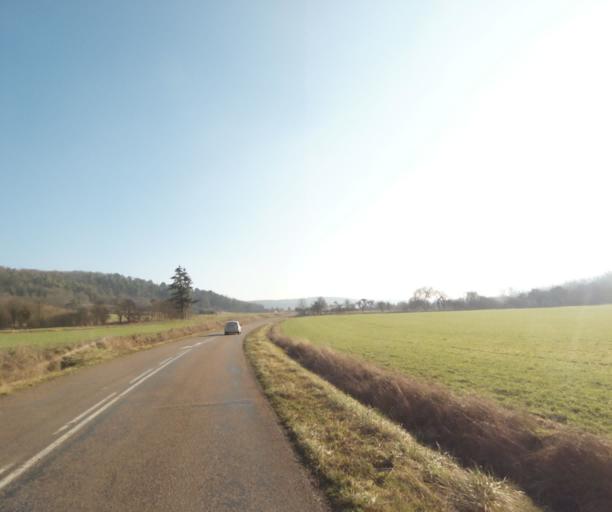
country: FR
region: Champagne-Ardenne
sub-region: Departement de la Haute-Marne
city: Chevillon
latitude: 48.4987
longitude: 5.1319
